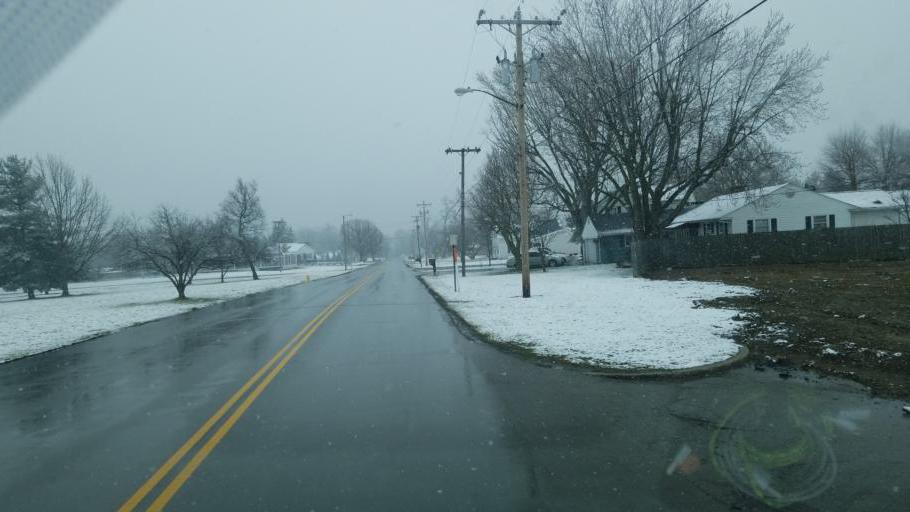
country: US
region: Indiana
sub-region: Grant County
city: Marion
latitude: 40.5739
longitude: -85.6733
